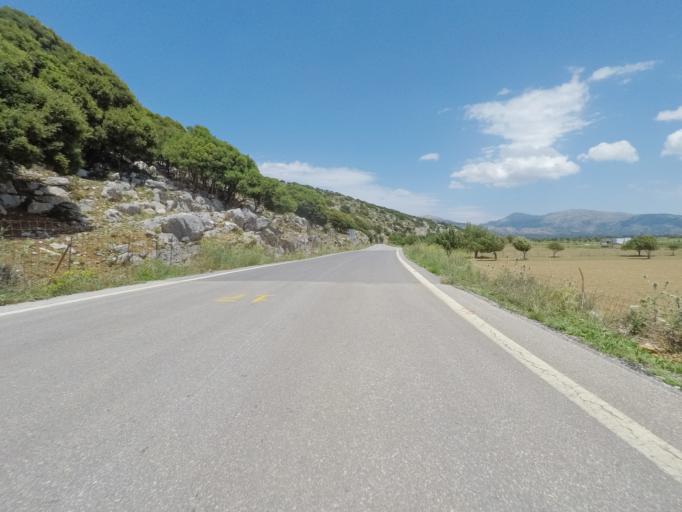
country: GR
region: Crete
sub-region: Nomos Irakleiou
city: Mokhos
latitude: 35.1958
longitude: 25.4489
